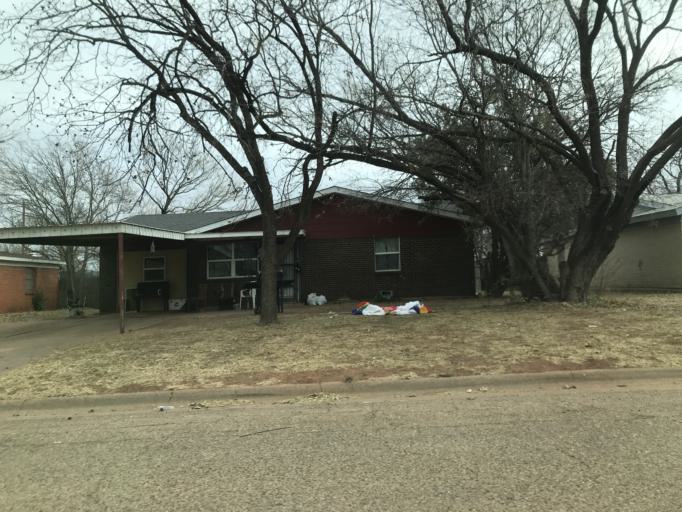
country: US
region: Texas
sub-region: Taylor County
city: Abilene
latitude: 32.4714
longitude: -99.7600
